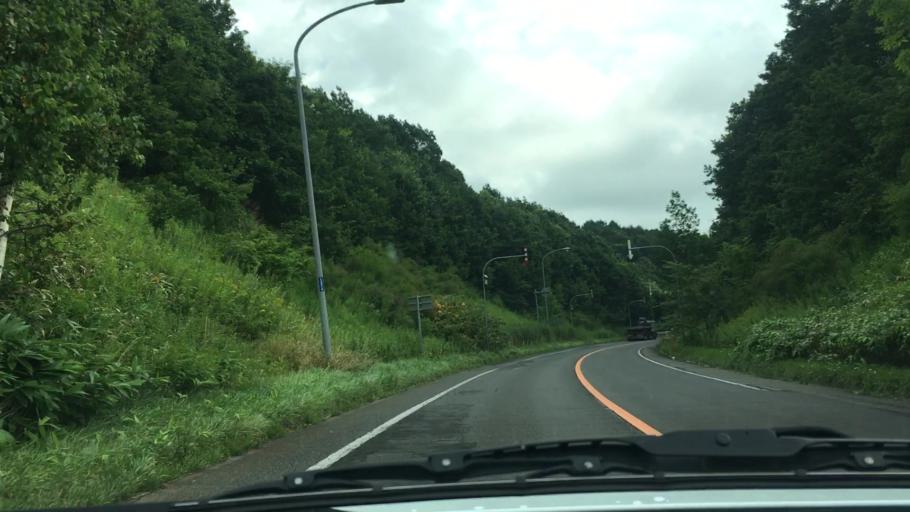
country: JP
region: Hokkaido
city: Chitose
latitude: 42.9454
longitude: 141.7384
